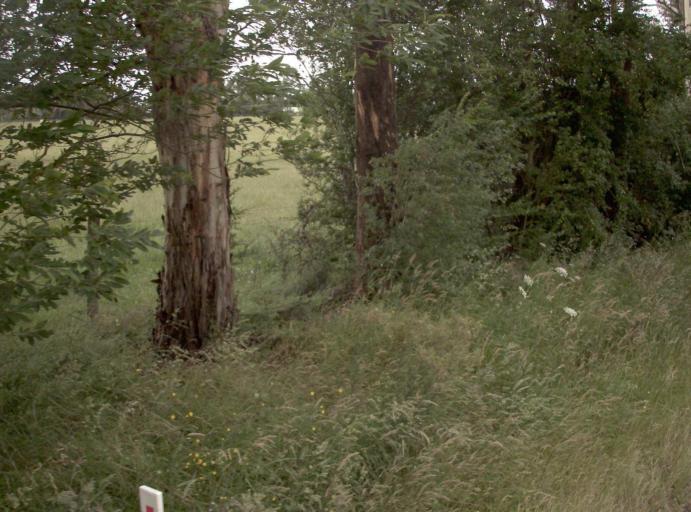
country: AU
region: Victoria
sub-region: Baw Baw
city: Warragul
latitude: -38.1645
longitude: 145.9756
